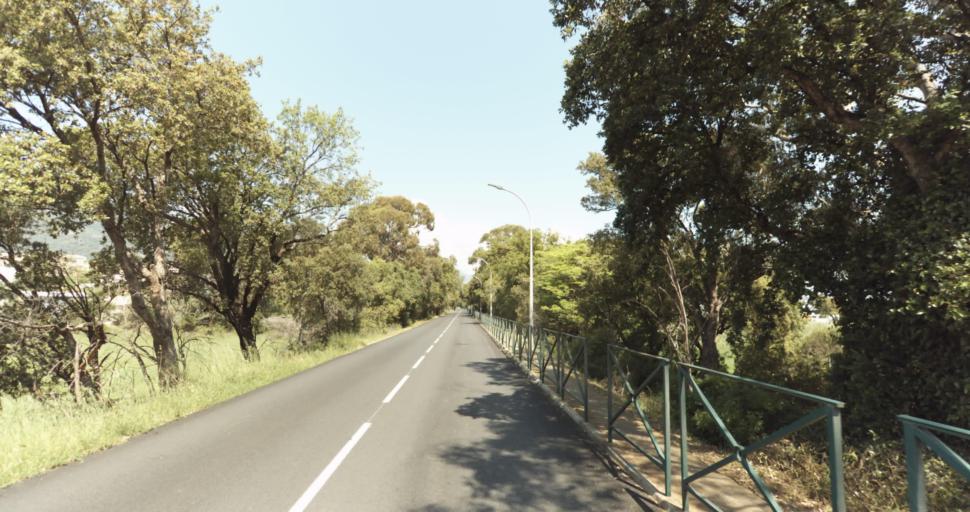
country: FR
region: Corsica
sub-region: Departement de la Haute-Corse
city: Biguglia
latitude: 42.6023
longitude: 9.4345
